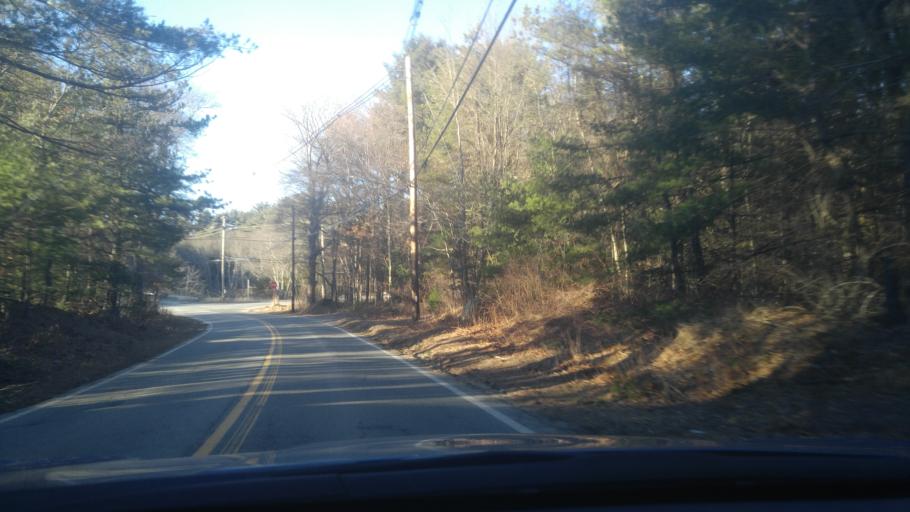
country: US
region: Rhode Island
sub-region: Kent County
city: West Warwick
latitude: 41.6486
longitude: -71.5730
